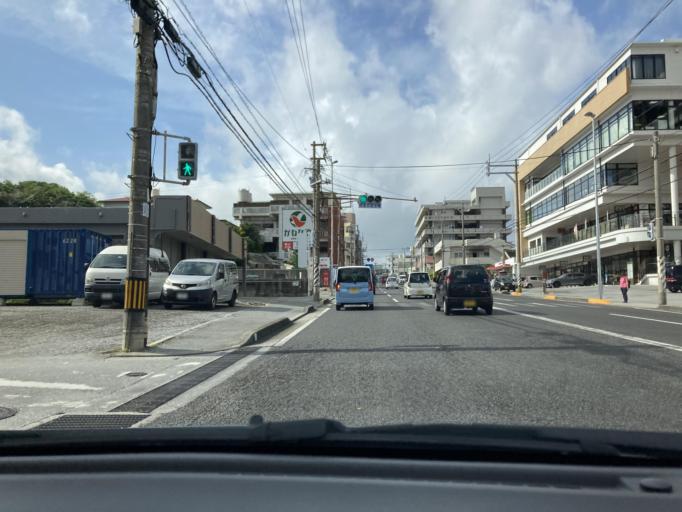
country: JP
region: Okinawa
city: Ginowan
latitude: 26.2565
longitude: 127.7407
